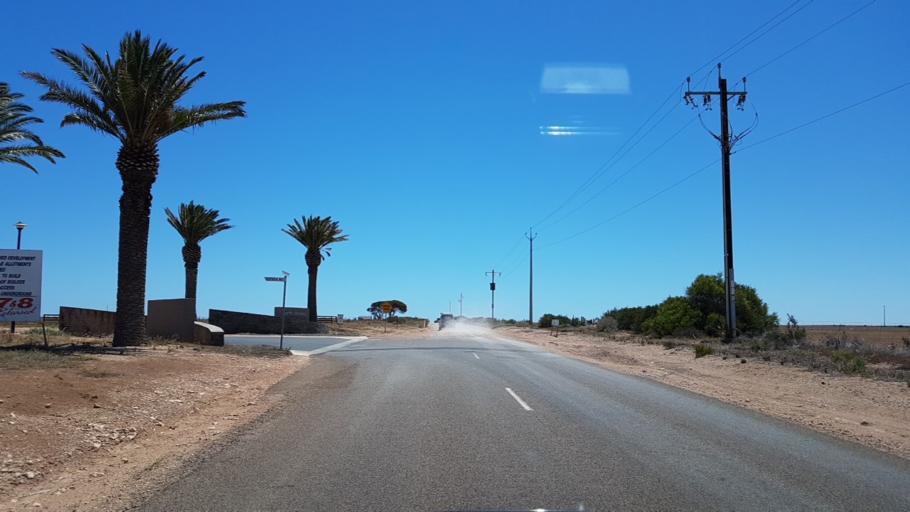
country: AU
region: South Australia
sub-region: Copper Coast
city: Wallaroo
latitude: -33.8917
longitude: 137.6343
